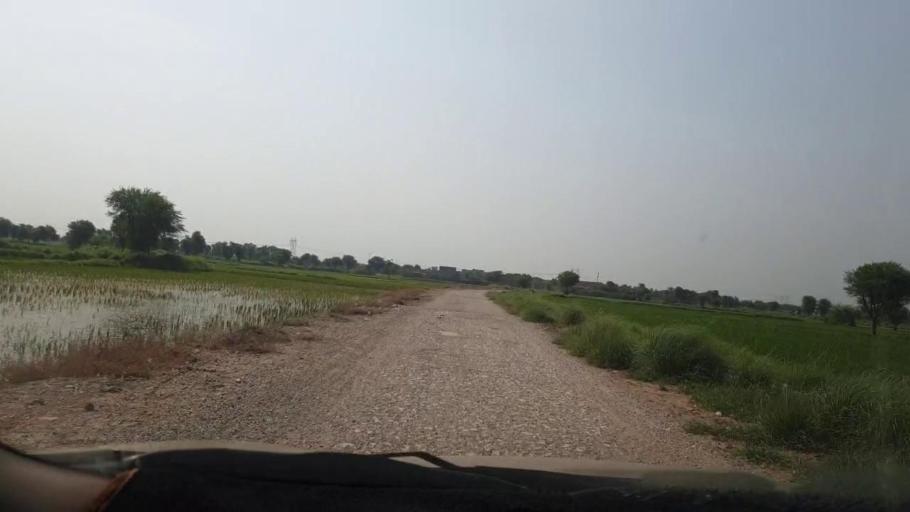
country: PK
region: Sindh
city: Goth Garelo
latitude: 27.4371
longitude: 68.0422
